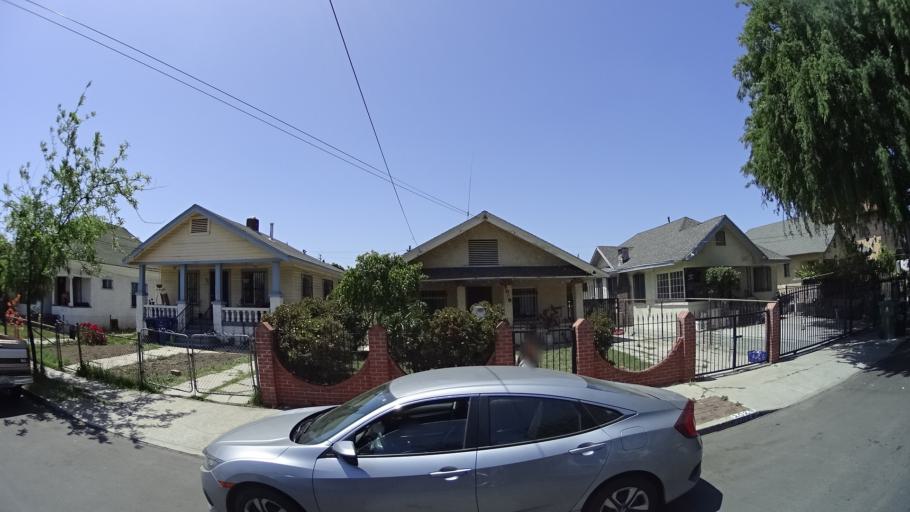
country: US
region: California
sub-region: Los Angeles County
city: Boyle Heights
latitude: 34.0685
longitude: -118.2103
